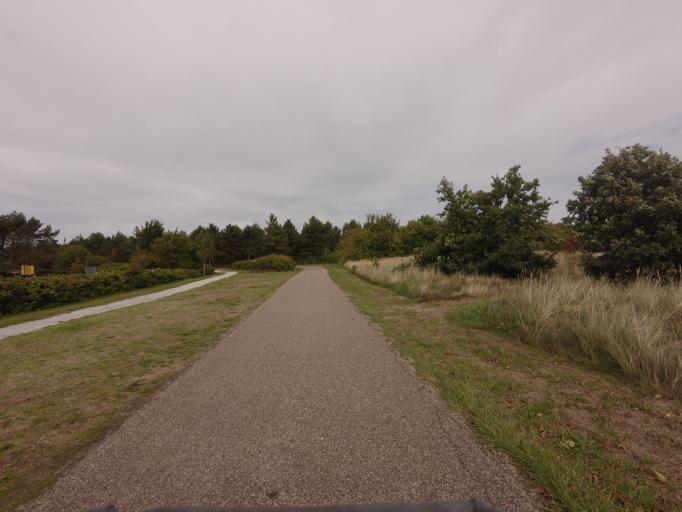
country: NL
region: Friesland
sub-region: Gemeente Ameland
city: Nes
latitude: 53.4517
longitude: 5.7816
